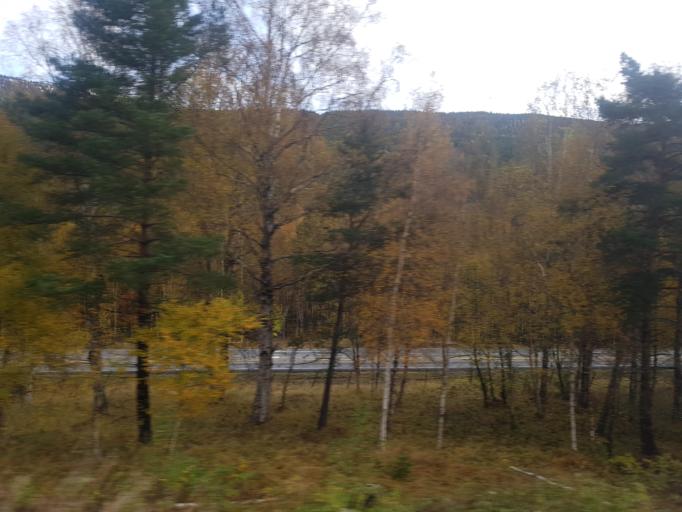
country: NO
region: Oppland
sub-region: Dovre
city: Dovre
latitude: 61.9138
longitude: 9.3505
